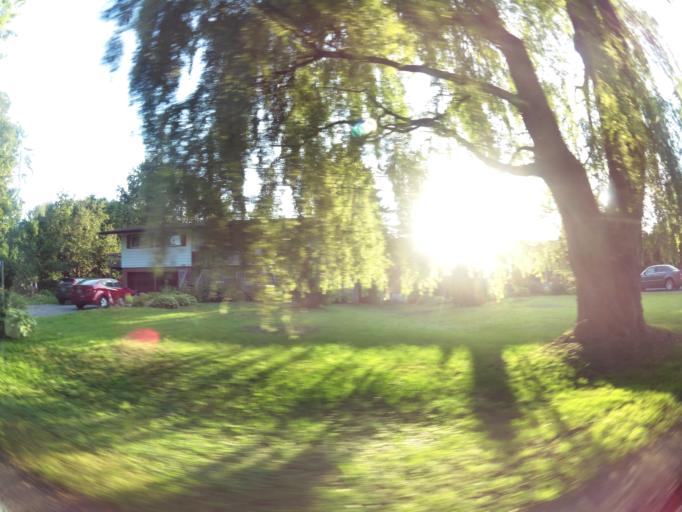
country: CA
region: Ontario
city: Clarence-Rockland
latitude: 45.5082
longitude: -75.4250
